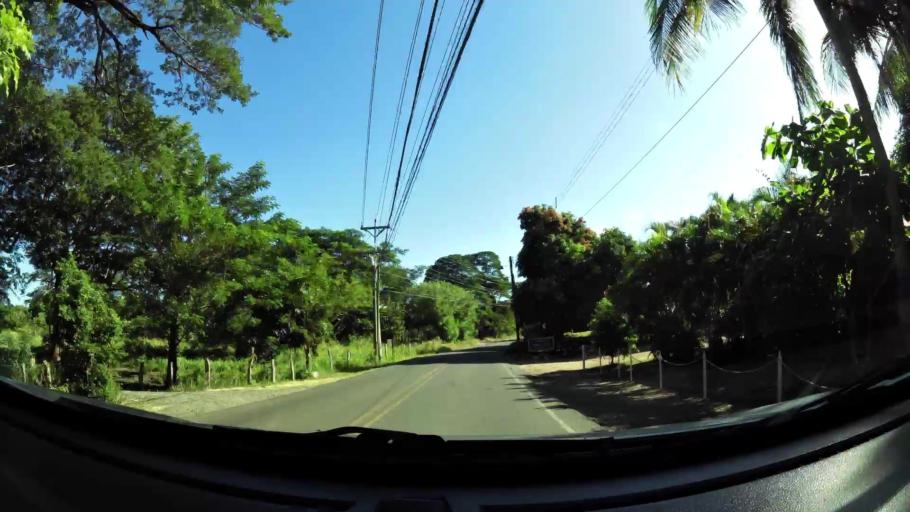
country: CR
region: Guanacaste
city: Sardinal
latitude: 10.4103
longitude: -85.7900
